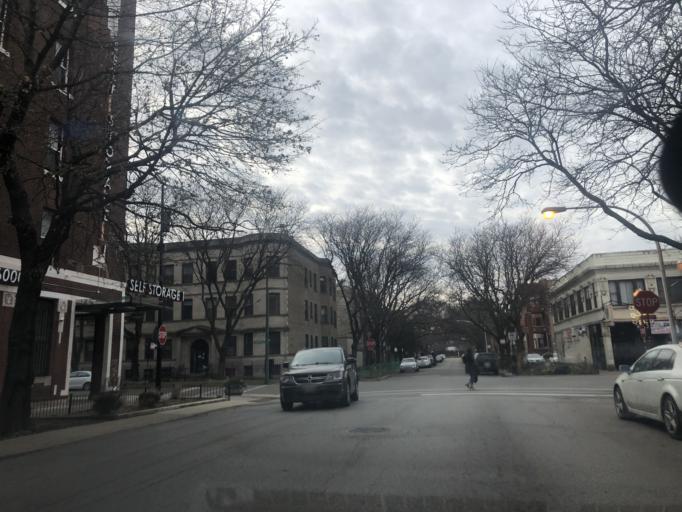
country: US
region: Illinois
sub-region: Cook County
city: Lincolnwood
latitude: 41.9527
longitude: -87.6540
